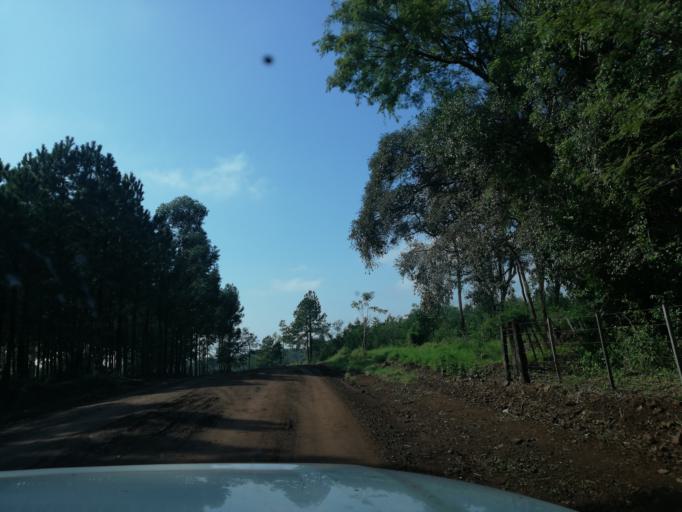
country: AR
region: Misiones
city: Cerro Azul
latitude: -27.6296
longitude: -55.5148
